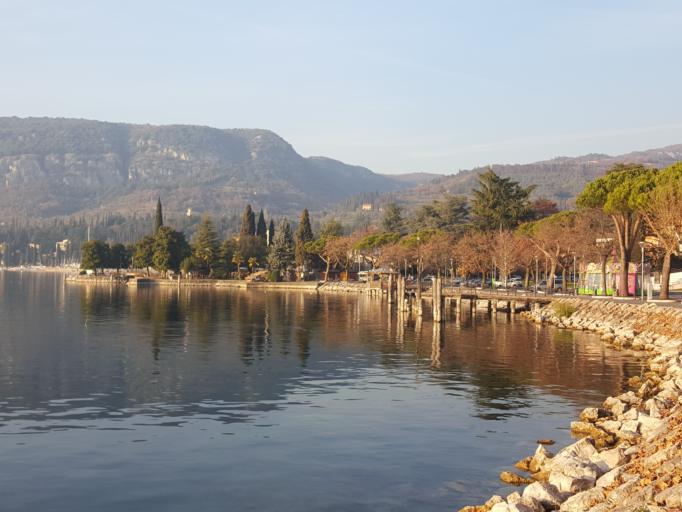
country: IT
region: Veneto
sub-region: Provincia di Verona
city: Garda
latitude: 45.5716
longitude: 10.7094
